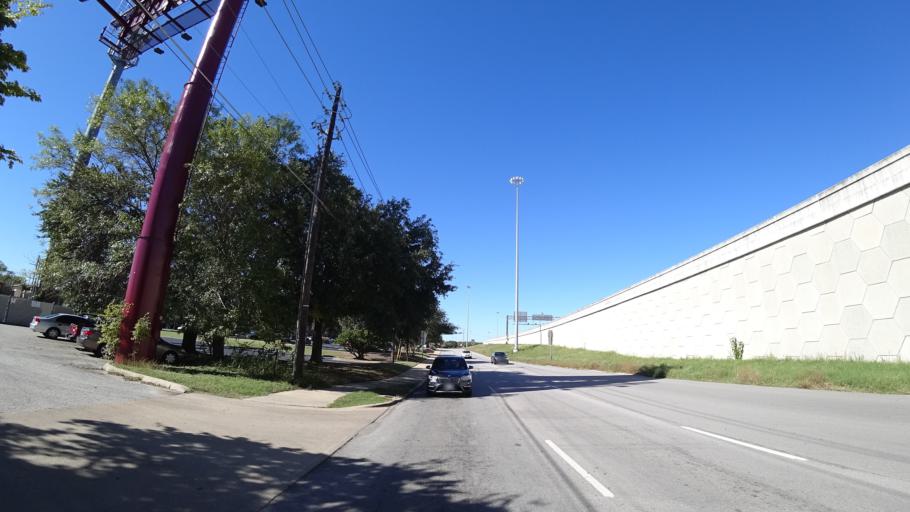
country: US
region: Texas
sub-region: Travis County
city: Rollingwood
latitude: 30.2318
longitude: -97.8015
